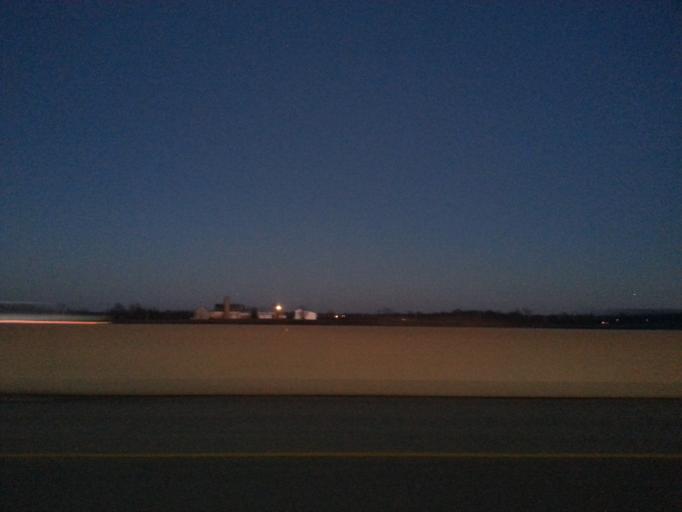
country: US
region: Indiana
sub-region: Lake County
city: Merrillville
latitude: 41.4405
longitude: -87.3216
